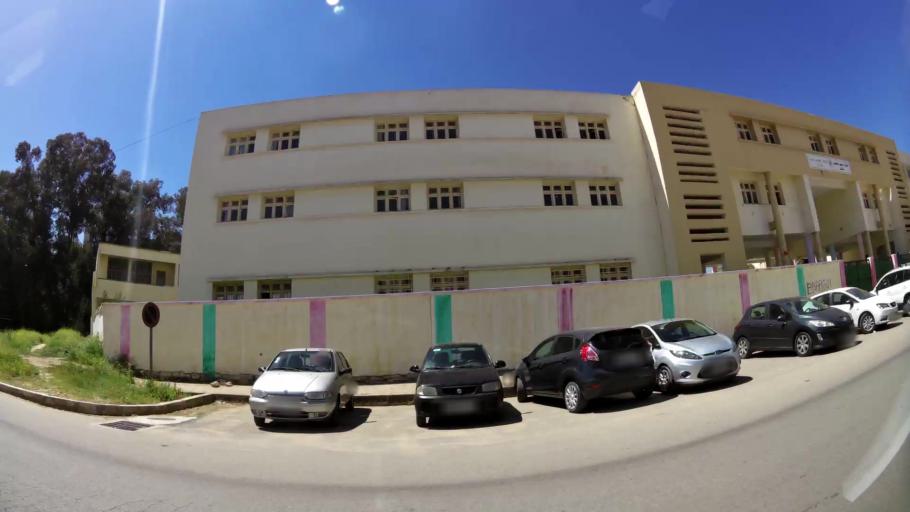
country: MA
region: Meknes-Tafilalet
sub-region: Meknes
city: Meknes
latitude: 33.9003
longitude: -5.5316
